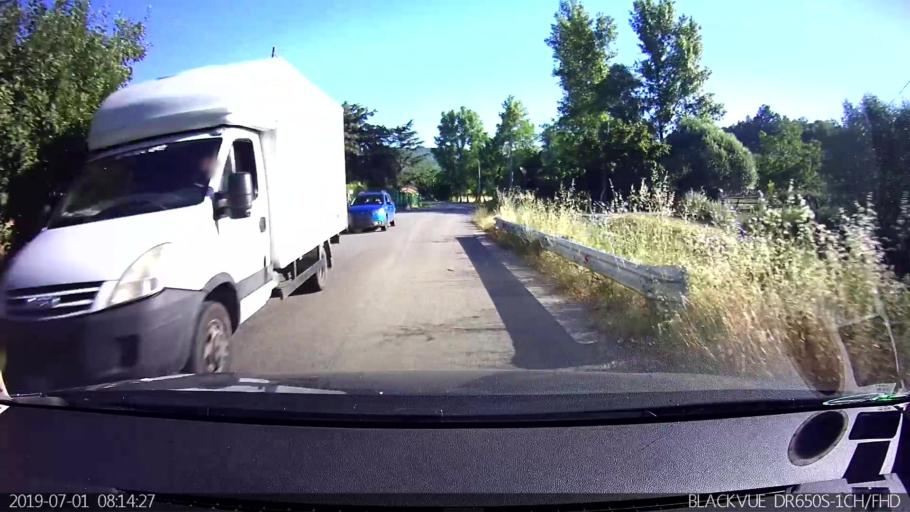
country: IT
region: Latium
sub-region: Provincia di Frosinone
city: Veroli
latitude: 41.6961
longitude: 13.4281
